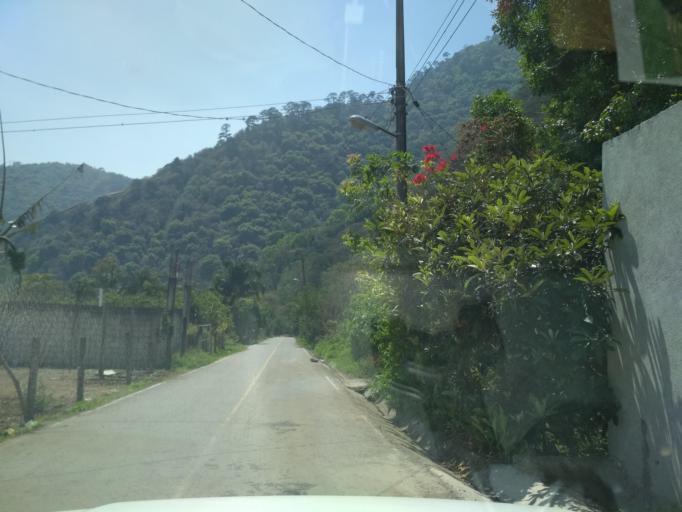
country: MX
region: Veracruz
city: Jalapilla
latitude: 18.8255
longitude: -97.1026
